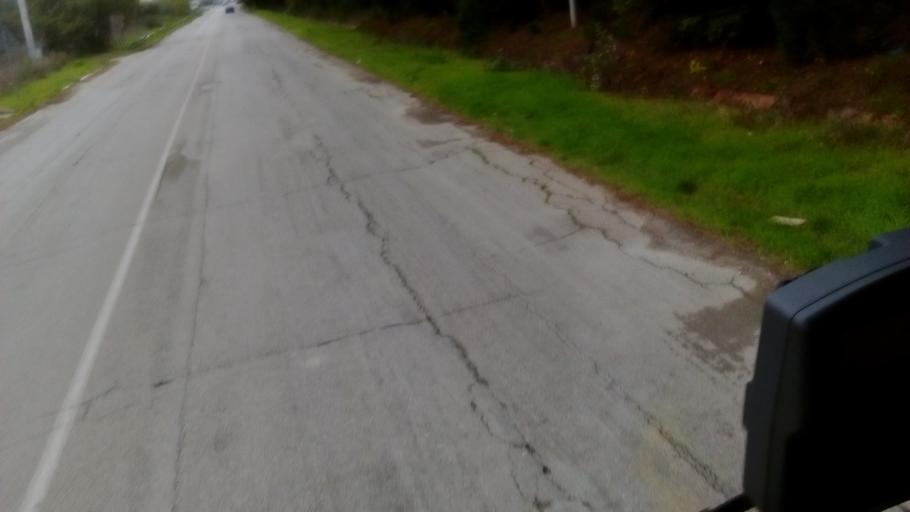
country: IT
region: Abruzzo
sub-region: Provincia di Chieti
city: San Salvo
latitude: 42.0409
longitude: 14.7509
